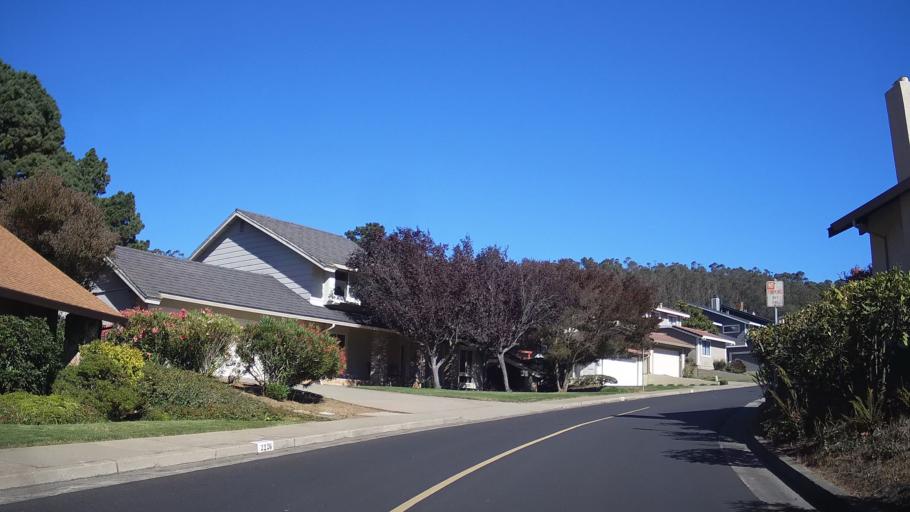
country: US
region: California
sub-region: Contra Costa County
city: East Richmond Heights
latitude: 37.9330
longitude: -122.3013
